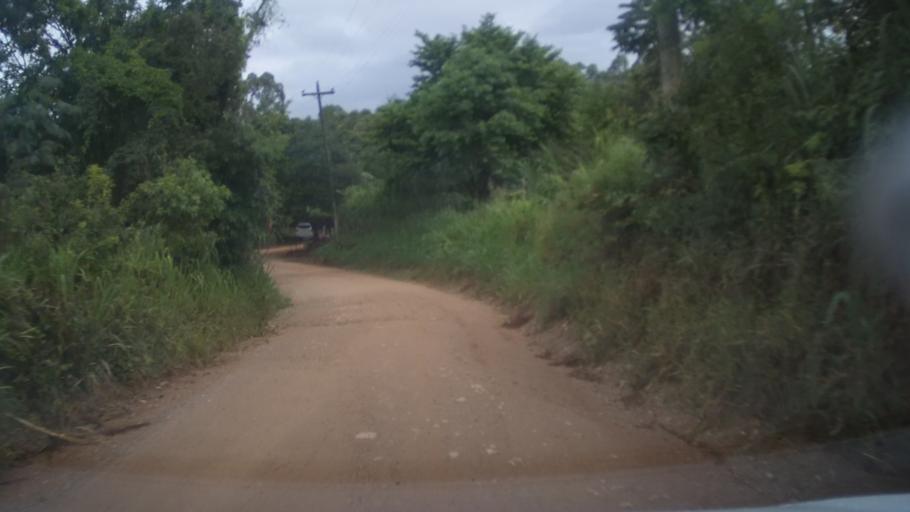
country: BR
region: Sao Paulo
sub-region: Itupeva
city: Itupeva
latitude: -23.1704
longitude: -47.0718
